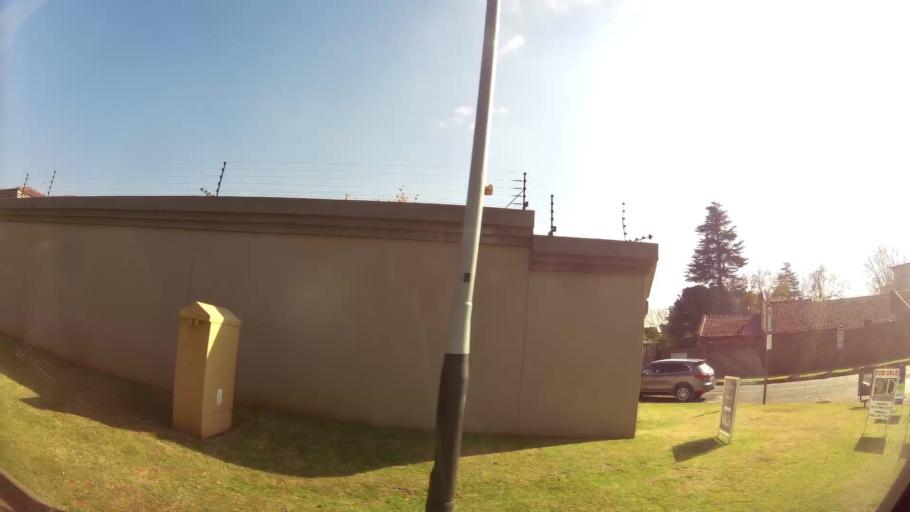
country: ZA
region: Gauteng
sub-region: Ekurhuleni Metropolitan Municipality
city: Germiston
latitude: -26.1806
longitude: 28.1441
